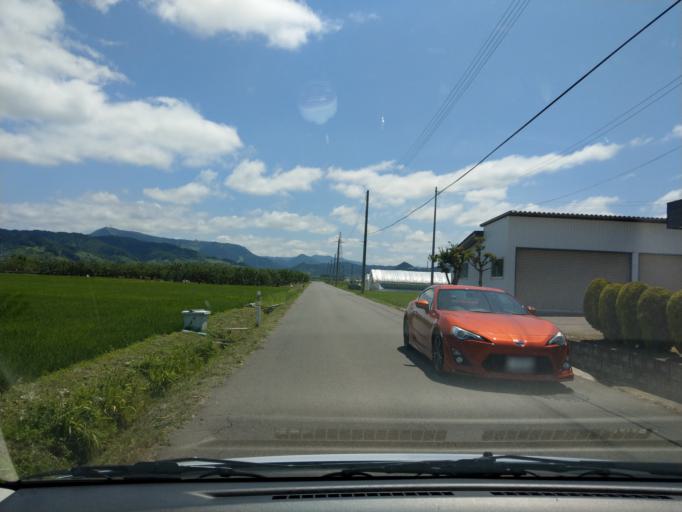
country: JP
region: Aomori
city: Hirosaki
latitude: 40.5636
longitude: 140.5515
